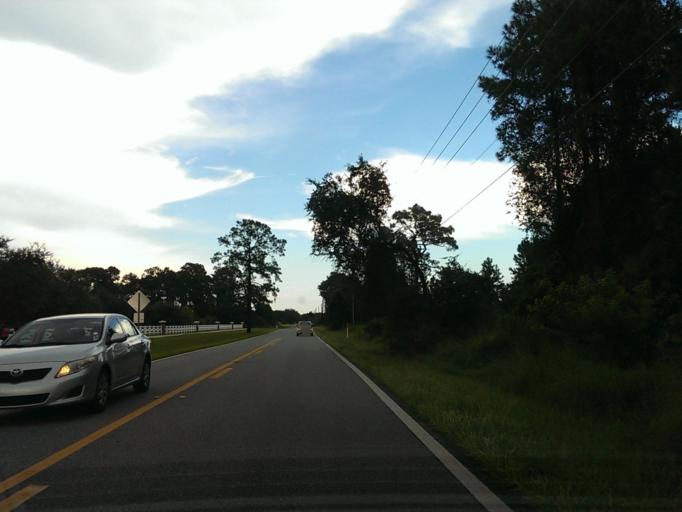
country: US
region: Florida
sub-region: Orange County
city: Bay Hill
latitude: 28.4302
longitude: -81.5672
